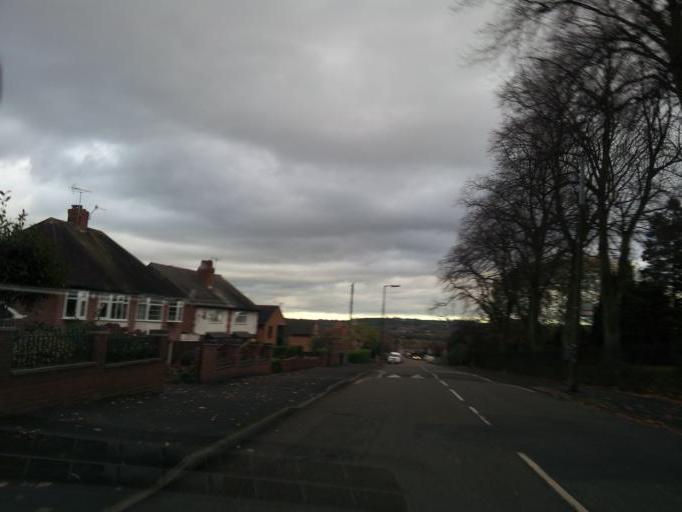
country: GB
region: England
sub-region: Nottinghamshire
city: Eastwood
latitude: 52.9901
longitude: -1.3163
